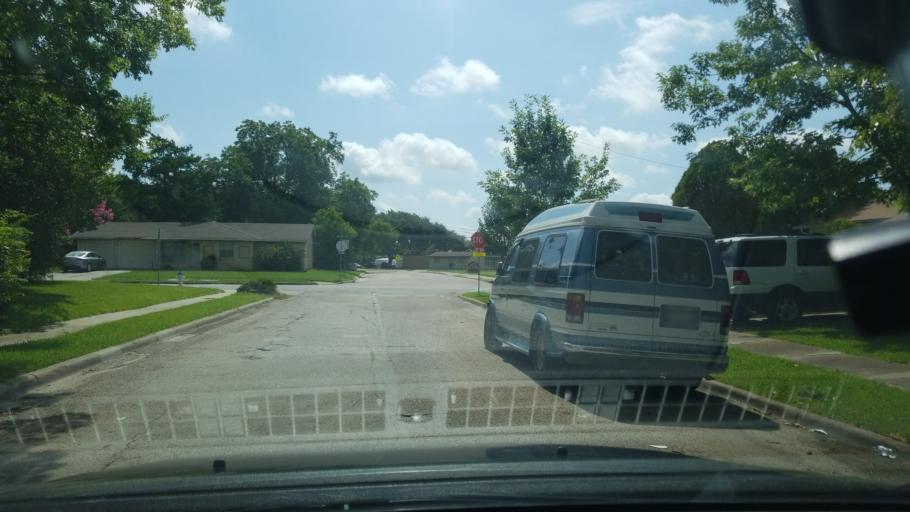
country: US
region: Texas
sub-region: Dallas County
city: Mesquite
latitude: 32.8173
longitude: -96.6500
